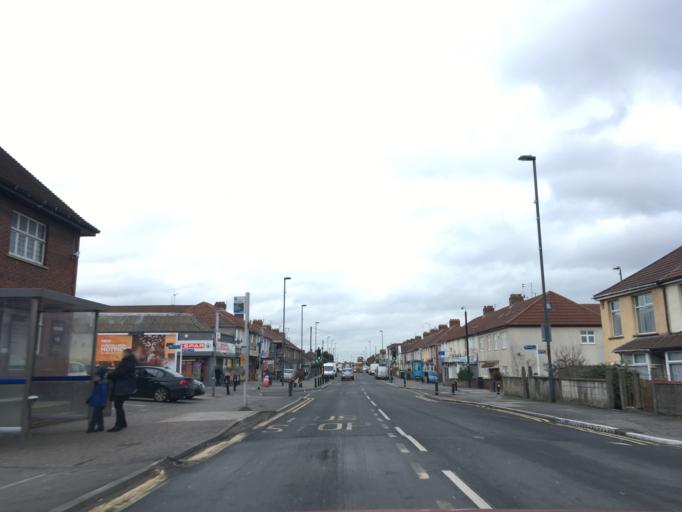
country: GB
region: England
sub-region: South Gloucestershire
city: Stoke Gifford
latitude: 51.5014
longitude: -2.5699
